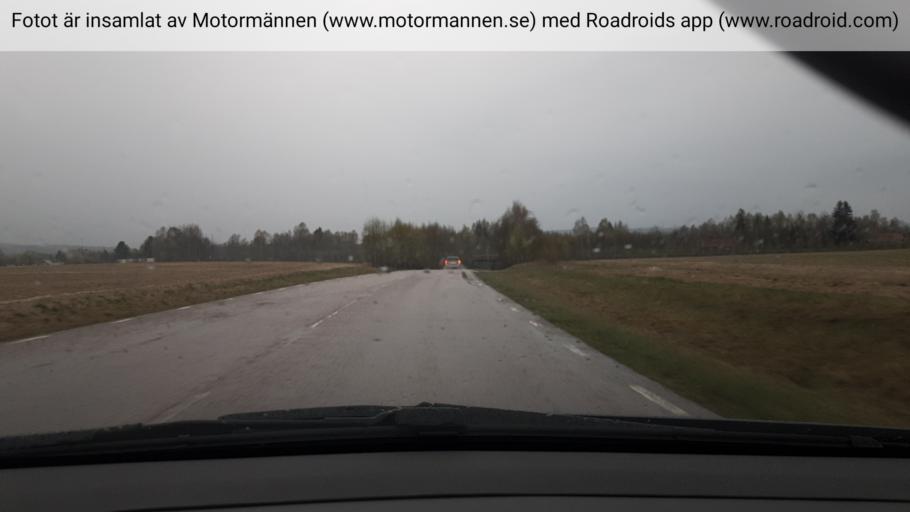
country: SE
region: Dalarna
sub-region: Borlange Kommun
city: Borlaenge
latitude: 60.4635
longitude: 15.3987
